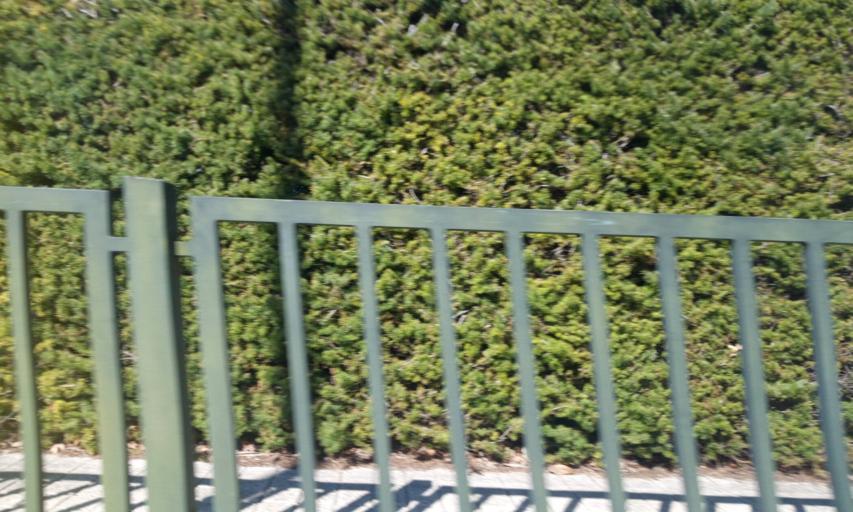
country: PT
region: Guarda
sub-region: Manteigas
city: Manteigas
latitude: 40.4887
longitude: -7.5965
